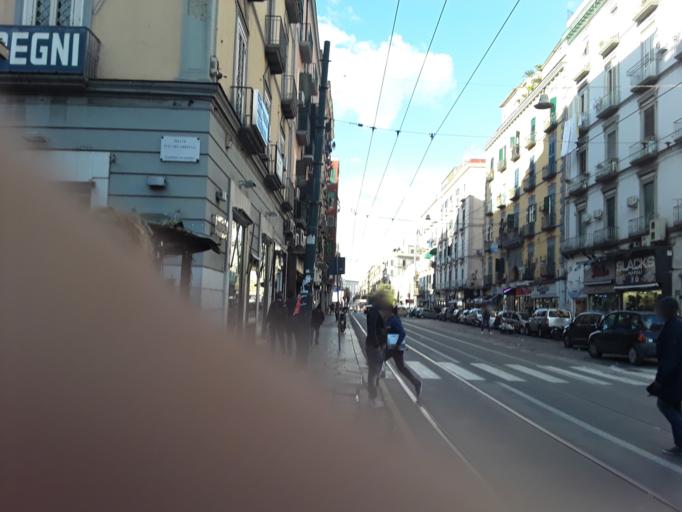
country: IT
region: Campania
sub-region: Provincia di Napoli
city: Napoli
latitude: 40.8541
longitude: 14.2677
